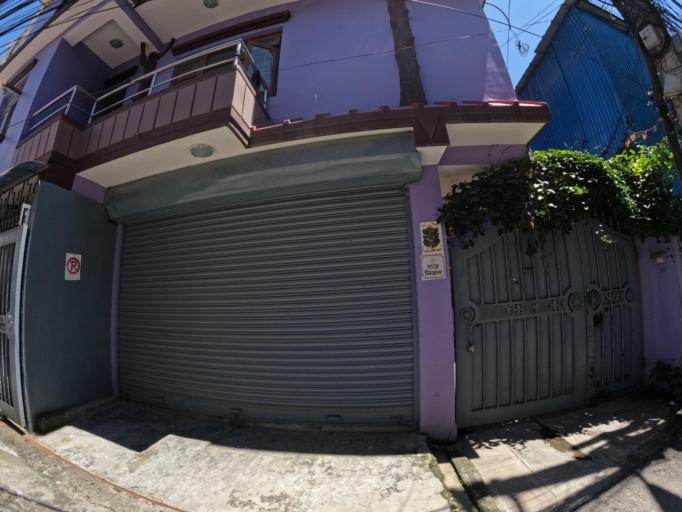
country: NP
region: Central Region
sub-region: Bagmati Zone
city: Kathmandu
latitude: 27.7460
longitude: 85.3255
